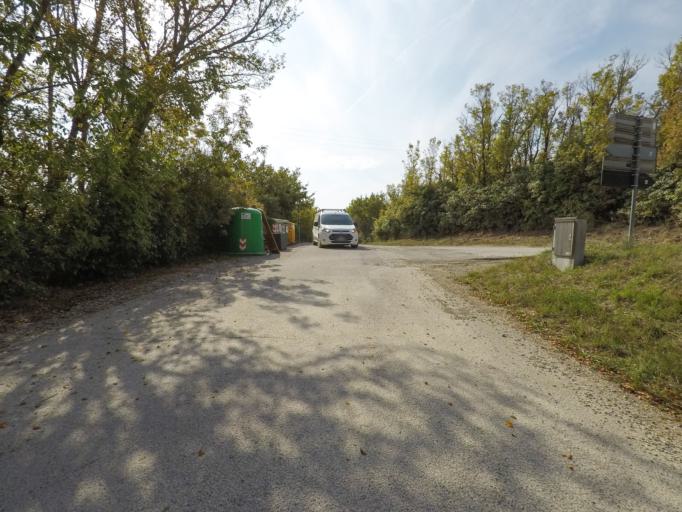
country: IT
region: Tuscany
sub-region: Provincia di Siena
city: Castellina in Chianti
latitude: 43.4278
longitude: 11.3348
